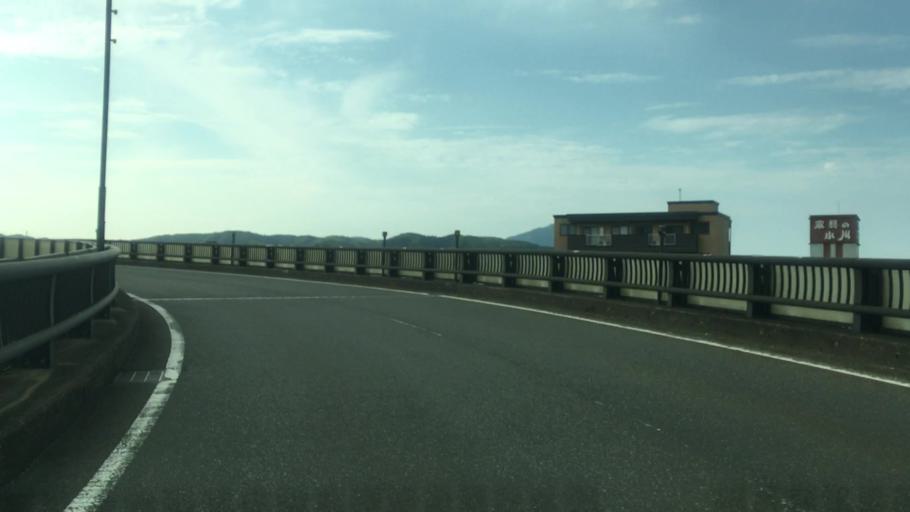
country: JP
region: Hyogo
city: Toyooka
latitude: 35.5477
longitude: 134.8125
